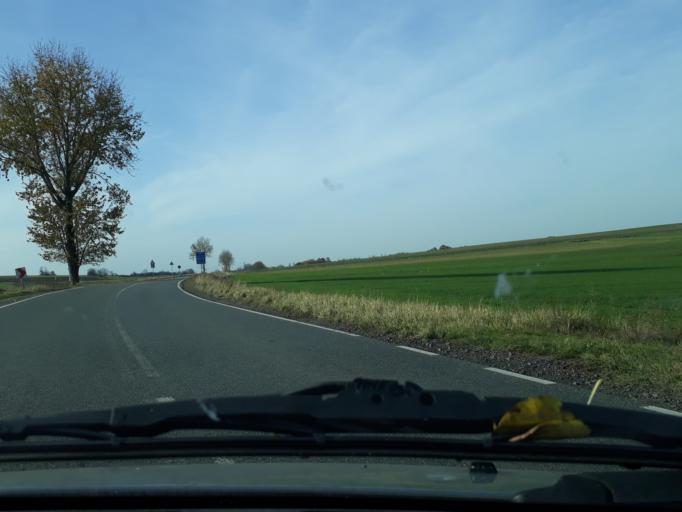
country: PL
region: Silesian Voivodeship
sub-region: Powiat myszkowski
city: Gniazdow
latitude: 50.5902
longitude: 19.0969
